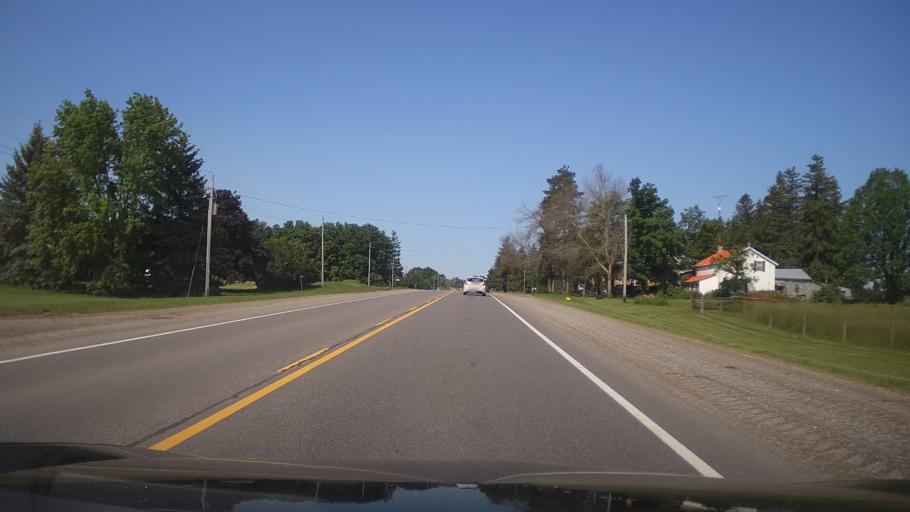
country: CA
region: Ontario
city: Omemee
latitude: 44.3415
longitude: -78.8413
